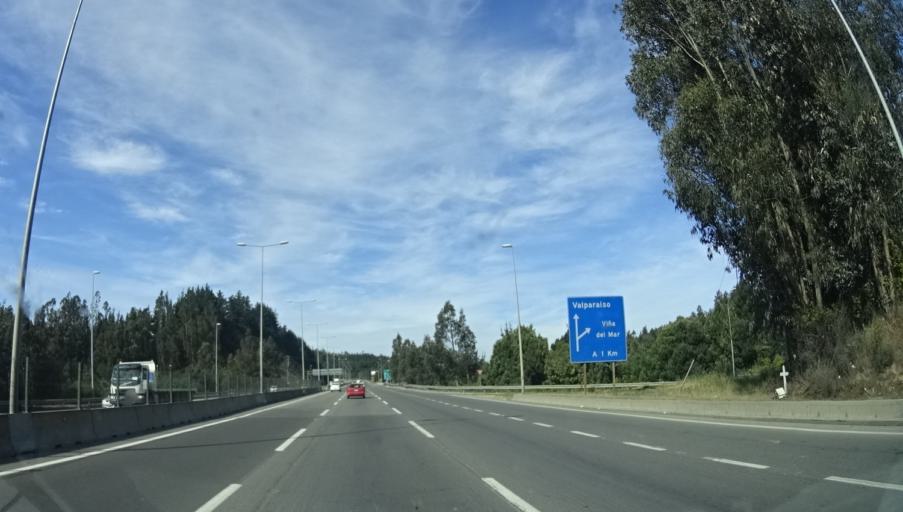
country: CL
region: Valparaiso
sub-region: Provincia de Valparaiso
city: Vina del Mar
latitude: -33.1091
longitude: -71.5568
